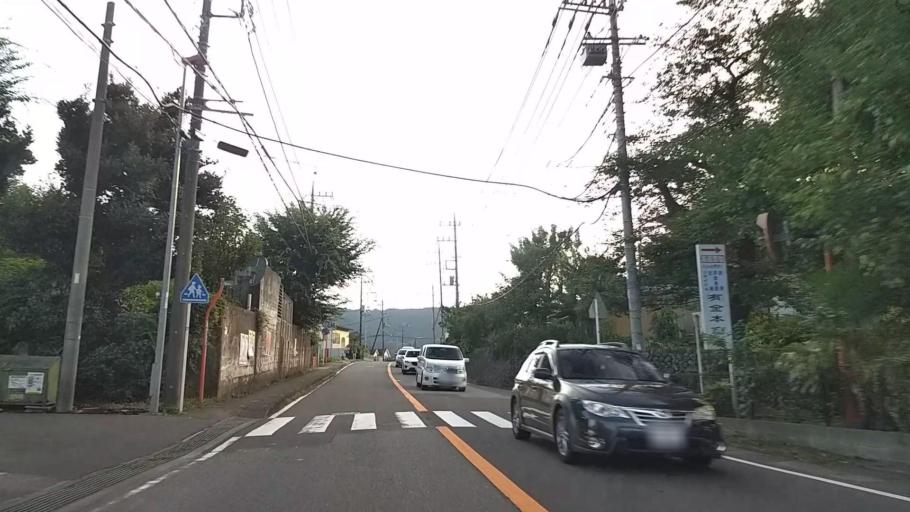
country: JP
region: Tokyo
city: Hachioji
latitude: 35.5690
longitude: 139.2624
